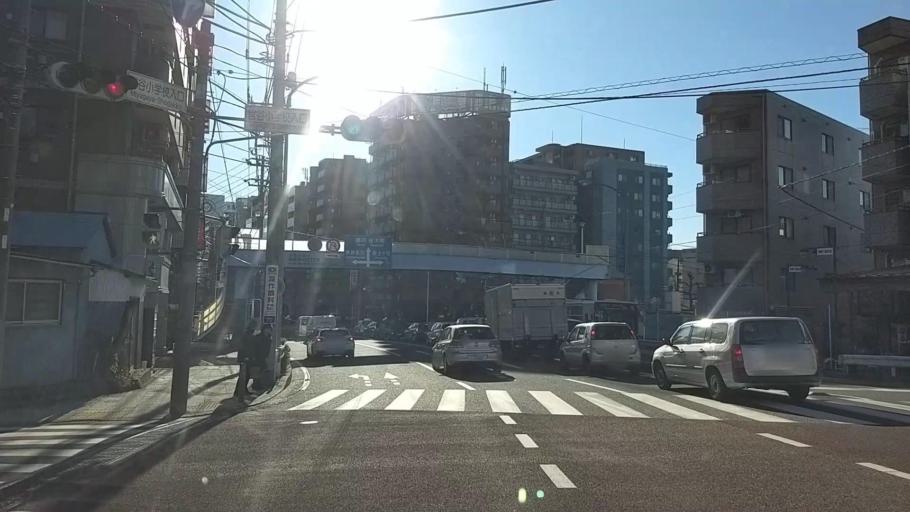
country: JP
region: Kanagawa
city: Yokohama
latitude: 35.4660
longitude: 139.6115
